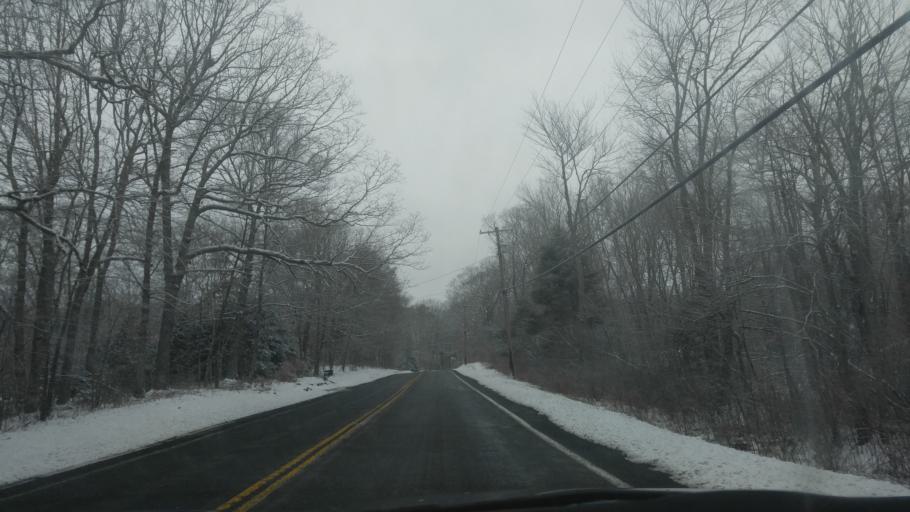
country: US
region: Rhode Island
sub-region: Providence County
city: Foster
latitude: 41.8179
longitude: -71.7389
